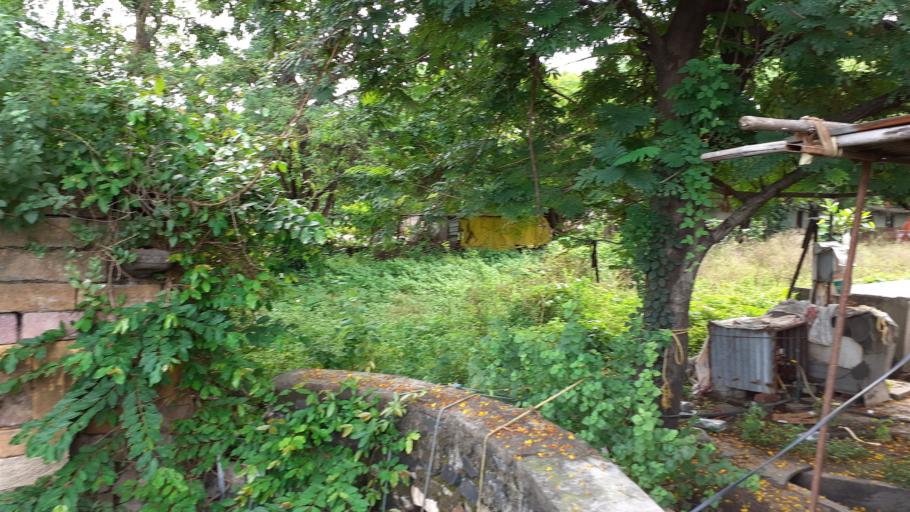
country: IN
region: Maharashtra
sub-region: Nagpur Division
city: Nagpur
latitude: 21.1371
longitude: 79.1216
